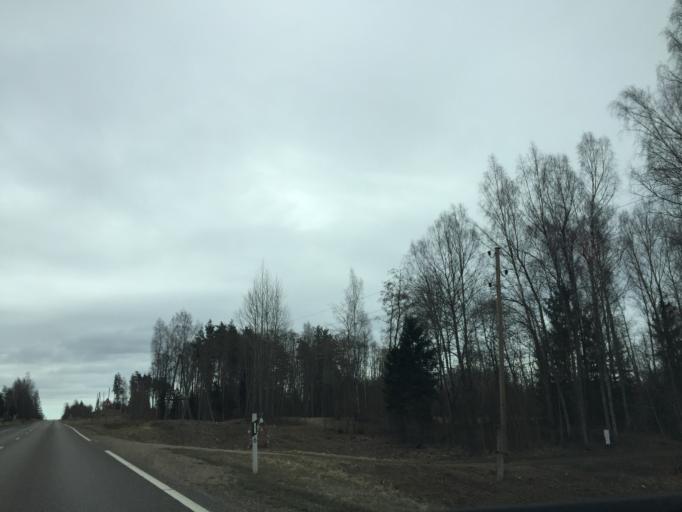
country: LV
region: Kraslavas Rajons
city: Kraslava
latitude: 55.9074
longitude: 27.1001
